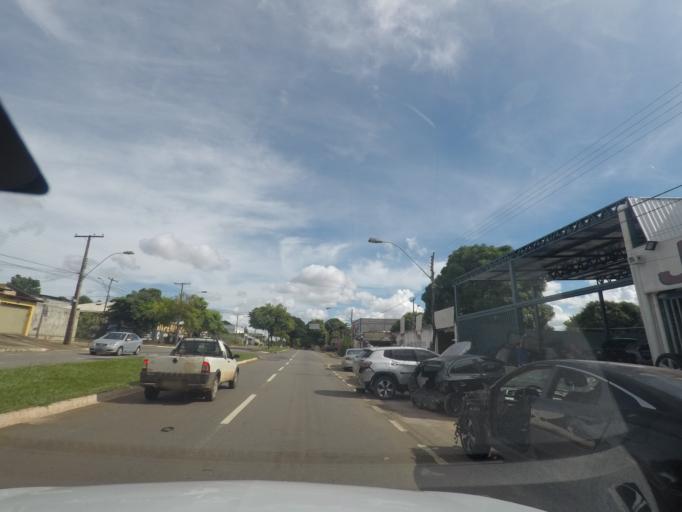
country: BR
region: Goias
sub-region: Goiania
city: Goiania
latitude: -16.7004
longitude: -49.3173
